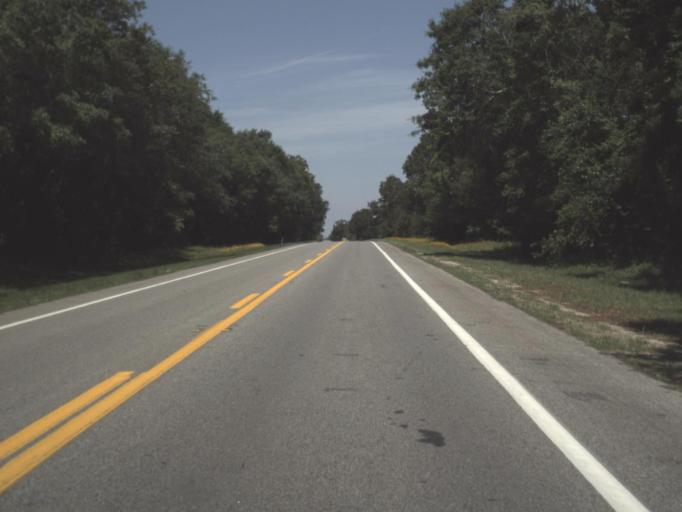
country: US
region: Florida
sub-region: Suwannee County
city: Live Oak
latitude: 30.3348
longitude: -83.0711
